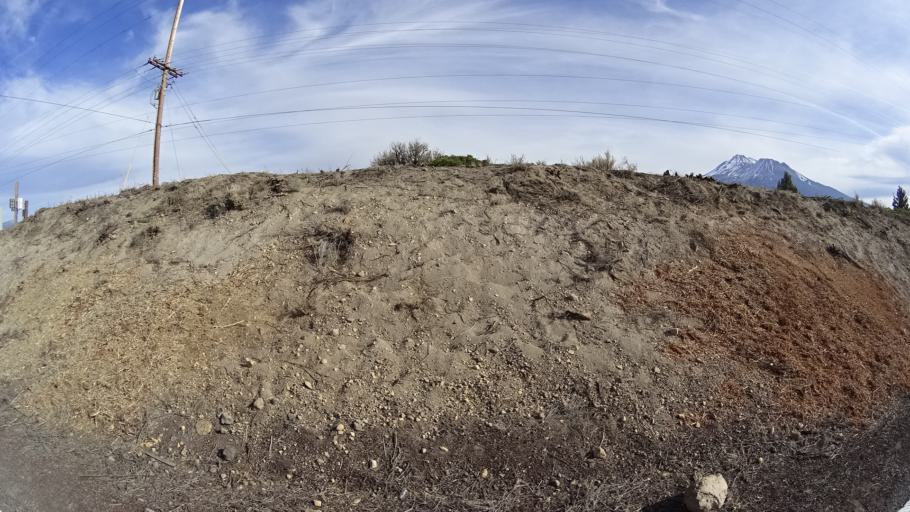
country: US
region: California
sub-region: Siskiyou County
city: Weed
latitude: 41.4938
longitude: -122.3624
